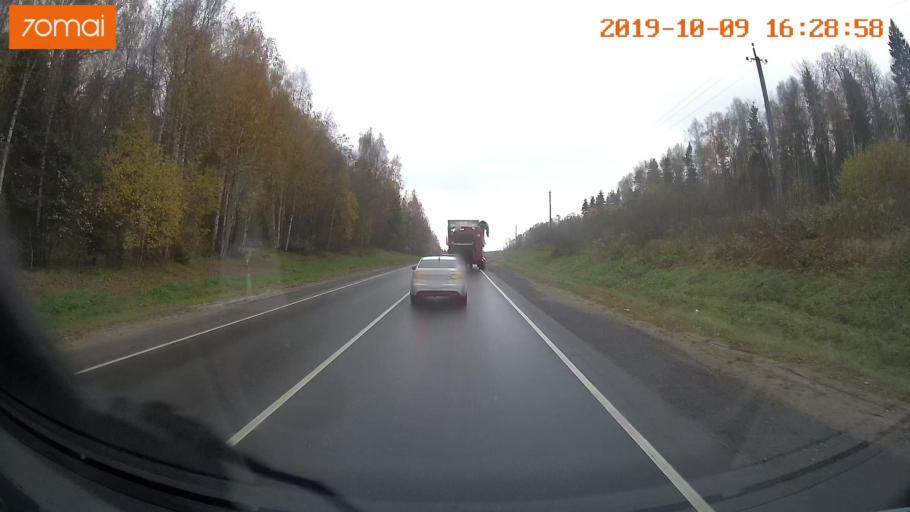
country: RU
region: Kostroma
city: Oktyabr'skiy
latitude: 57.6263
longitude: 40.9341
